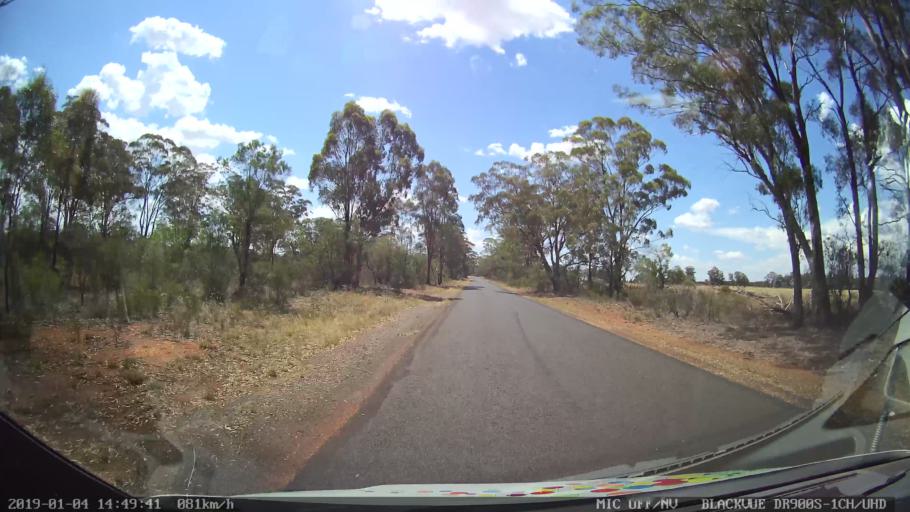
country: AU
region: New South Wales
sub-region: Dubbo Municipality
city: Dubbo
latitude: -32.0464
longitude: 148.6616
